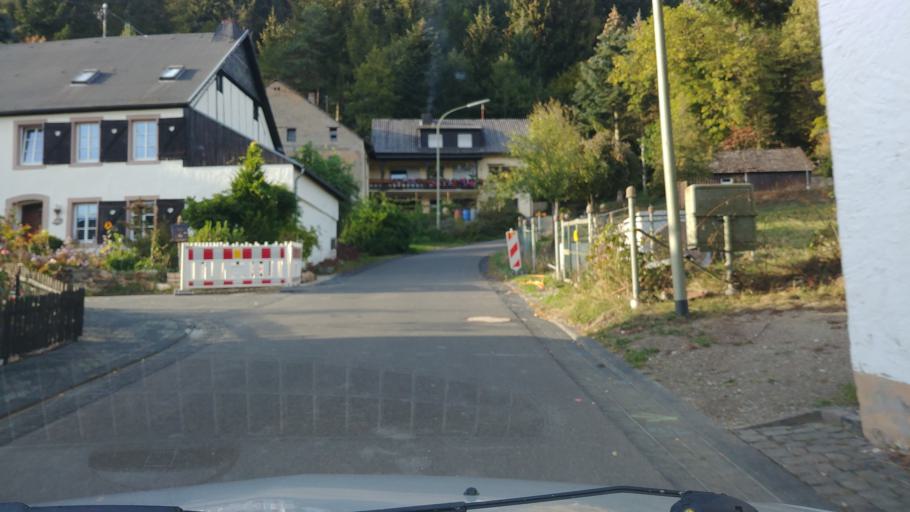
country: DE
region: Rheinland-Pfalz
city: Merschbach
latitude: 49.8037
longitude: 7.0053
